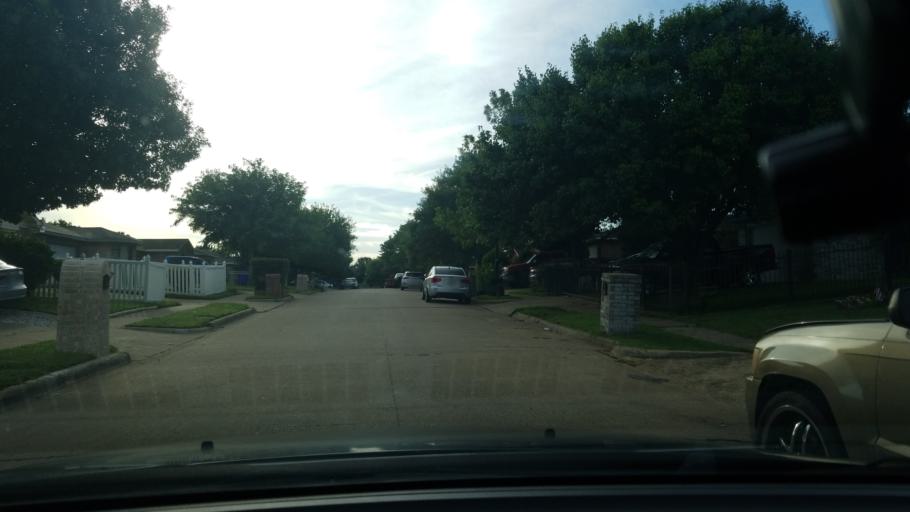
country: US
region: Texas
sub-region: Dallas County
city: Balch Springs
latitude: 32.7534
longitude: -96.6461
